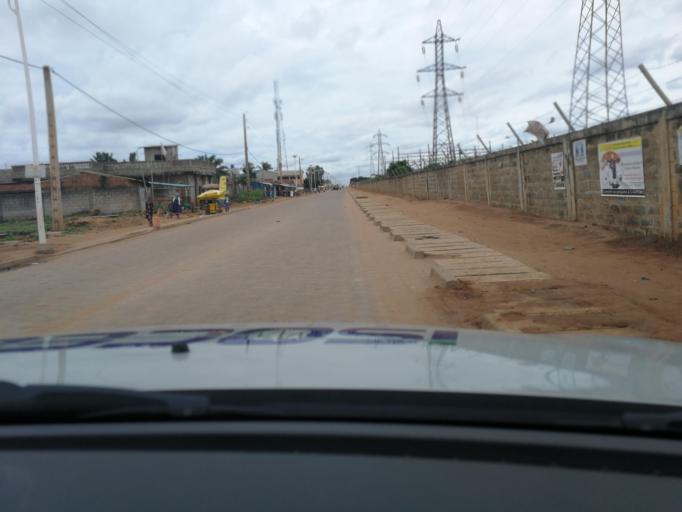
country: BJ
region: Atlantique
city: Abomey-Calavi
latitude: 6.4224
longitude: 2.3072
